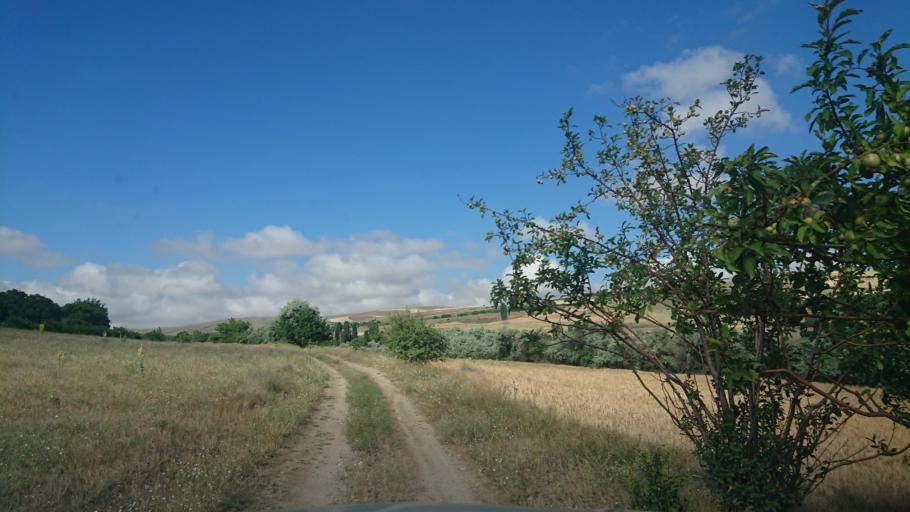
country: TR
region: Aksaray
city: Agacoren
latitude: 38.8514
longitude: 33.9348
